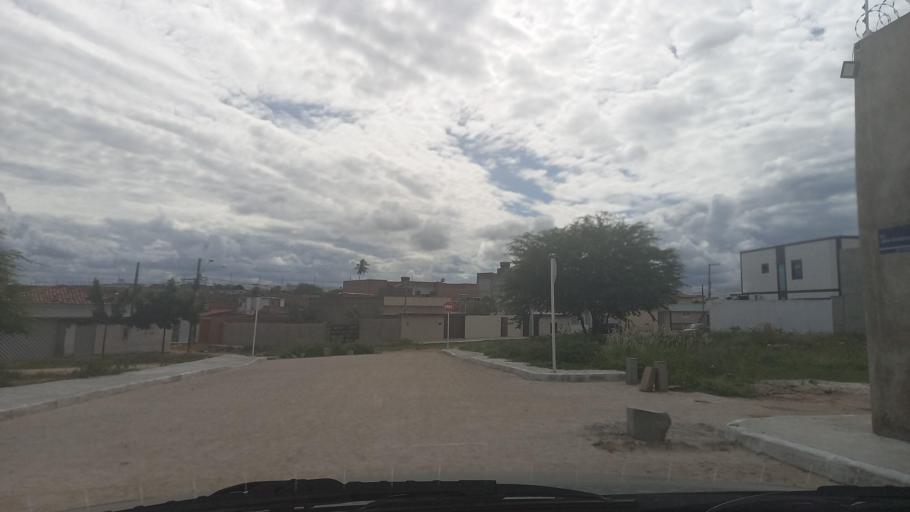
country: BR
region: Pernambuco
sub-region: Caruaru
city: Caruaru
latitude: -8.2922
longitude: -35.9916
